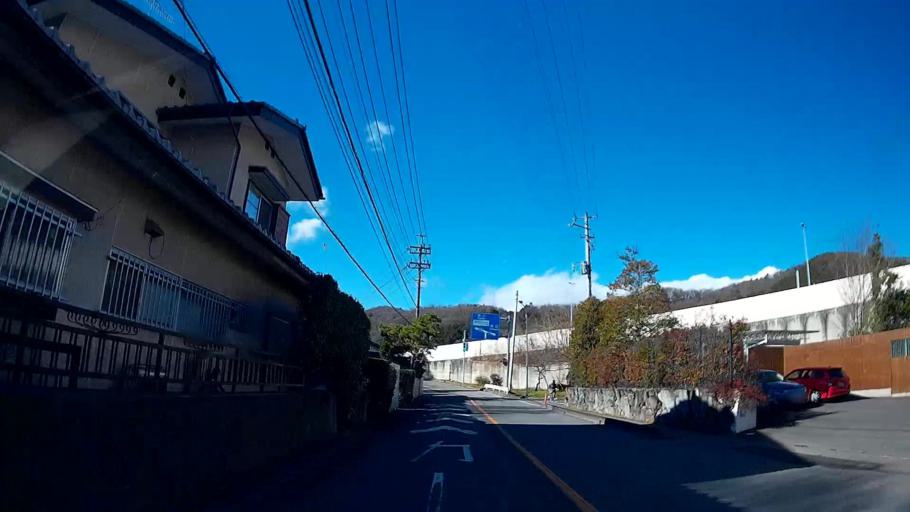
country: JP
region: Saitama
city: Yorii
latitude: 36.1195
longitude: 139.1811
